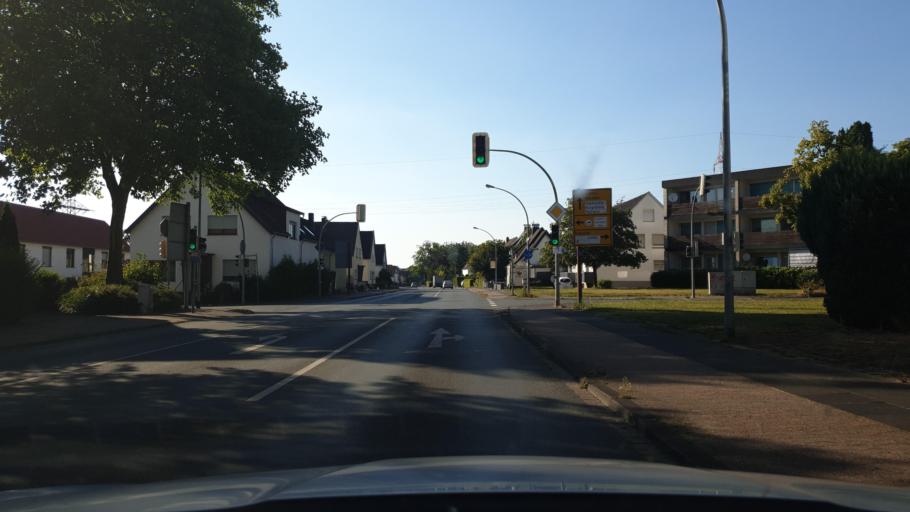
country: DE
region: North Rhine-Westphalia
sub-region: Regierungsbezirk Detmold
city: Bad Salzuflen
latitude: 52.0733
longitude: 8.7643
